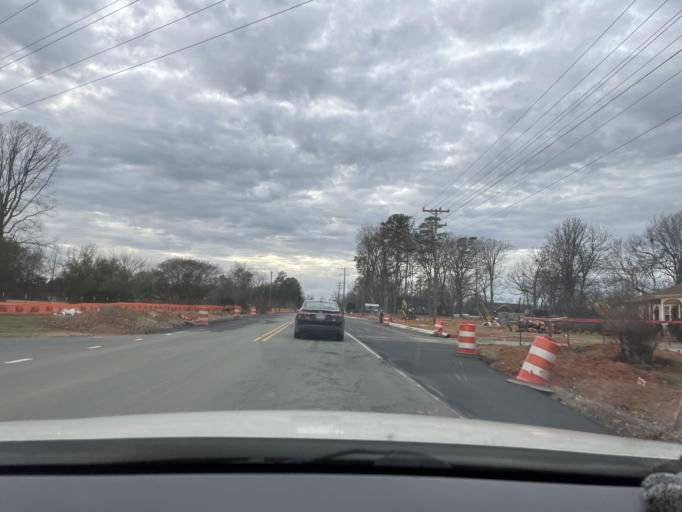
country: US
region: North Carolina
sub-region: Alamance County
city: Elon
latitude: 36.0731
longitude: -79.5071
